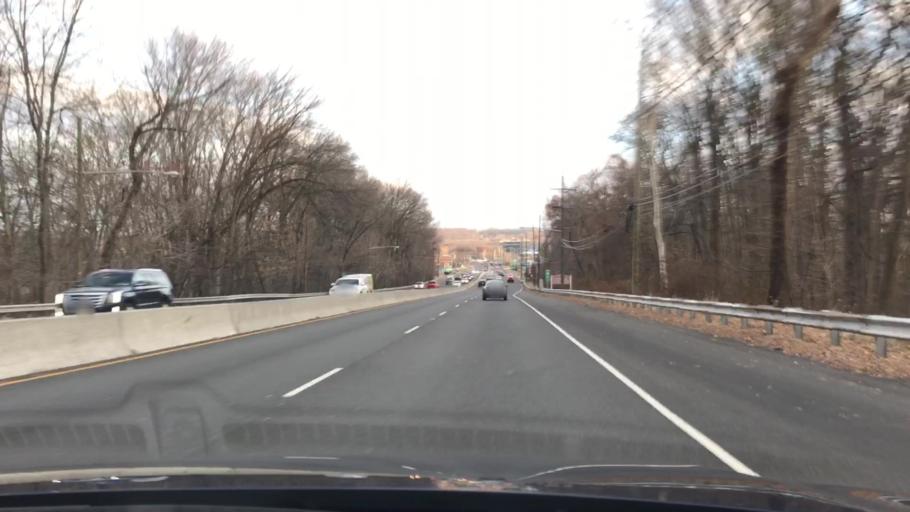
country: US
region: New Jersey
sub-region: Bergen County
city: Englewood
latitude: 40.8857
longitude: -73.9921
